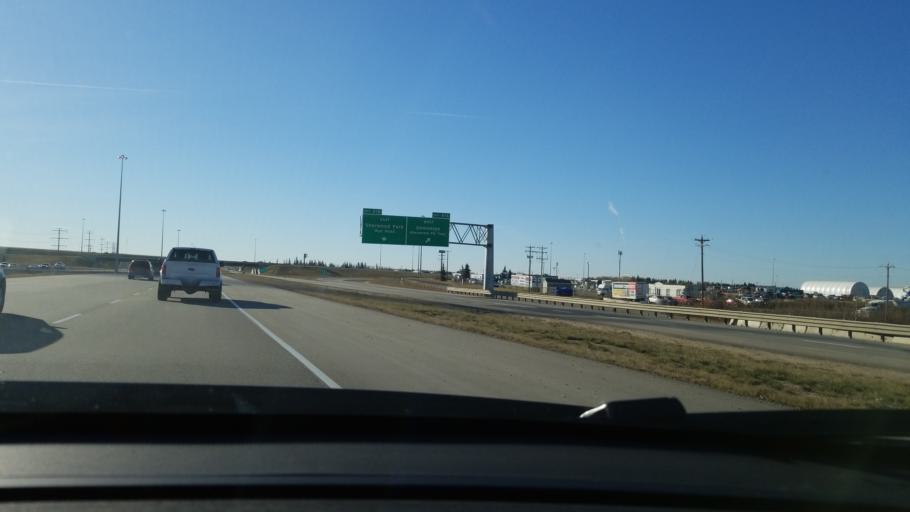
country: CA
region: Alberta
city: Sherwood Park
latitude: 53.5187
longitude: -113.3445
